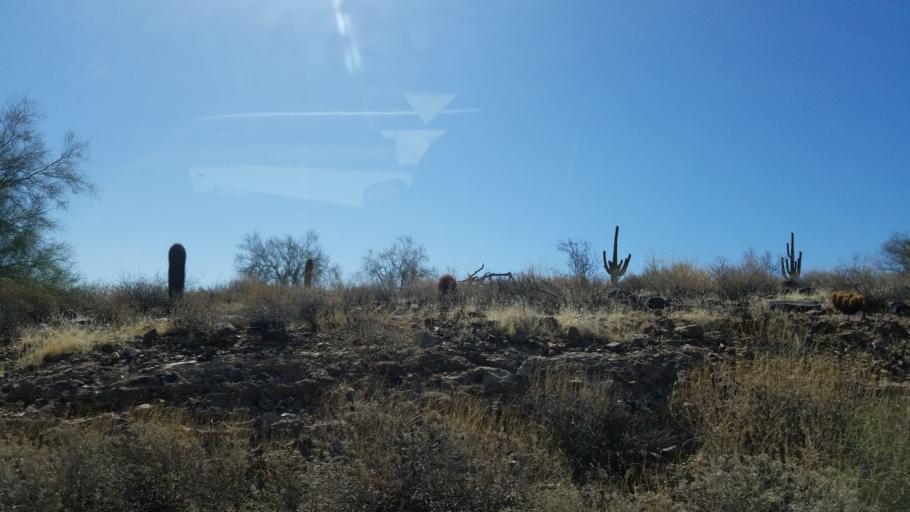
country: US
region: Arizona
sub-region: Maricopa County
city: Fountain Hills
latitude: 33.5853
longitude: -111.7564
